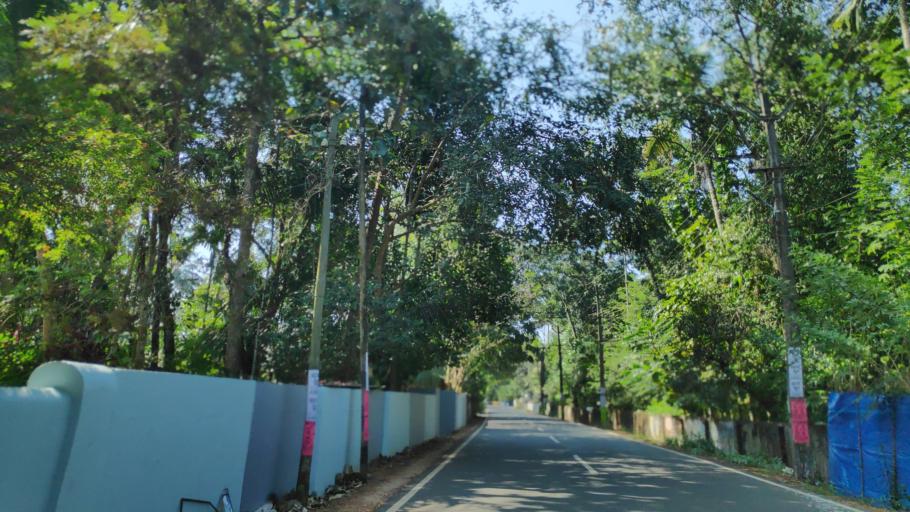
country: IN
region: Kerala
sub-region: Alappuzha
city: Shertallai
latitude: 9.6568
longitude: 76.3353
